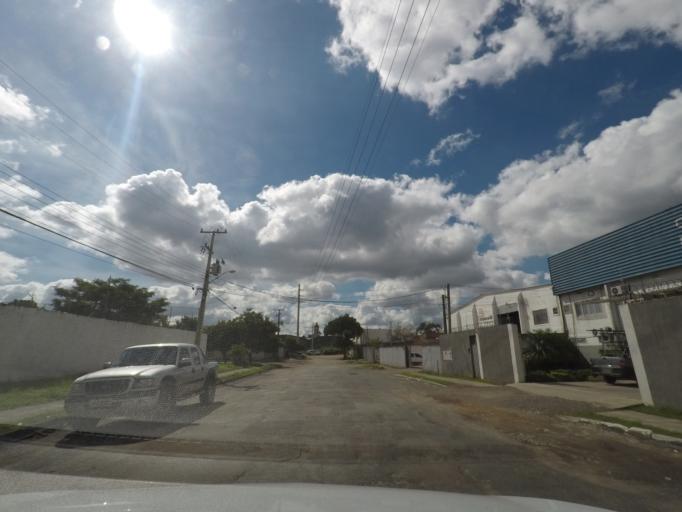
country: BR
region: Parana
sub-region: Sao Jose Dos Pinhais
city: Sao Jose dos Pinhais
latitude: -25.4934
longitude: -49.2292
